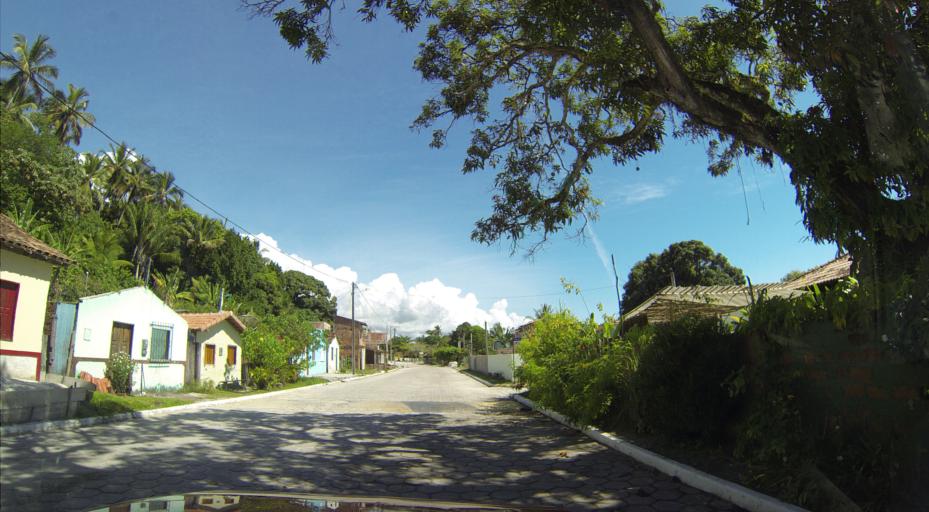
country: BR
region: Bahia
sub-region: Santa Cruz Cabralia
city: Santa Cruz Cabralia
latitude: -16.0876
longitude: -38.9524
